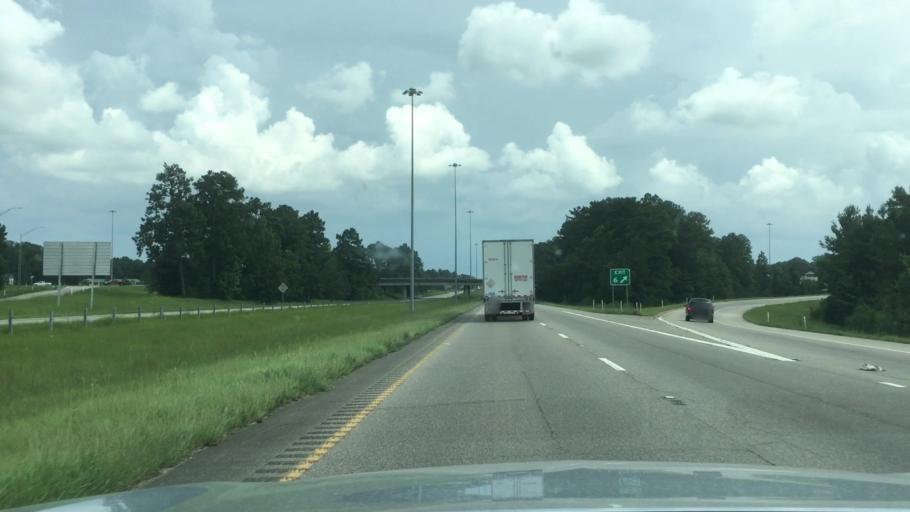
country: US
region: Mississippi
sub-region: Pearl River County
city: Picayune
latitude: 30.5402
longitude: -89.6513
